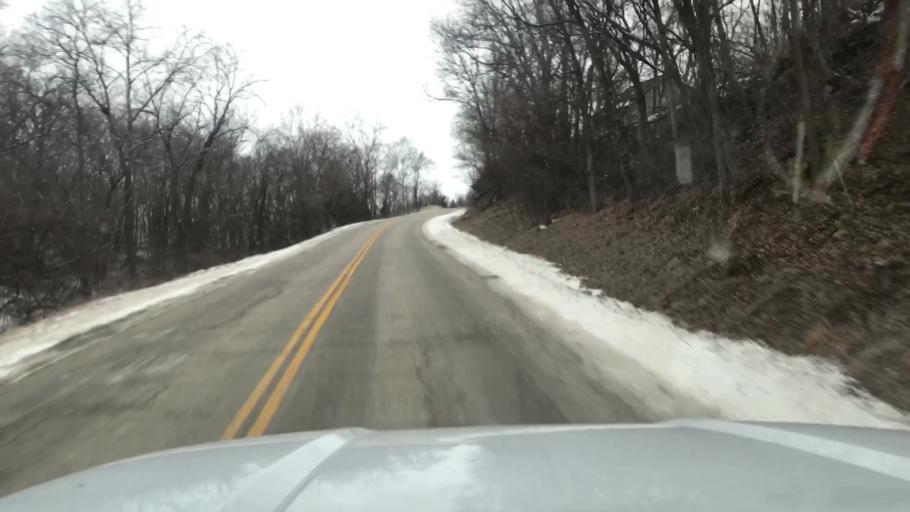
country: US
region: Missouri
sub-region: Andrew County
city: Savannah
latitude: 40.0239
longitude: -94.9174
